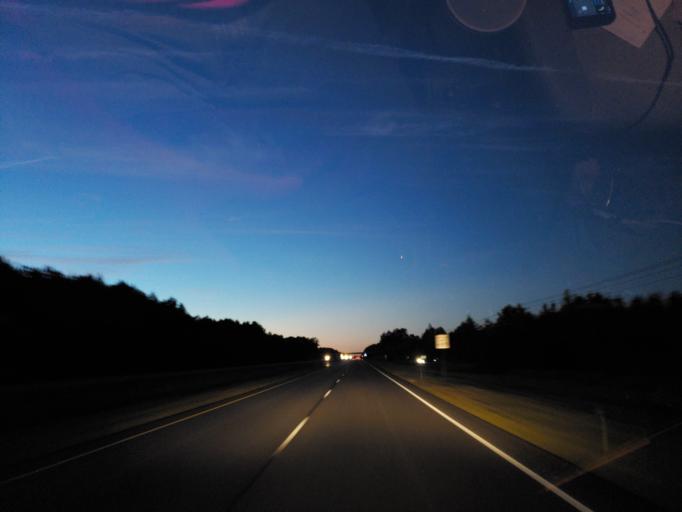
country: US
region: Mississippi
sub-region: Clarke County
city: Quitman
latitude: 32.0705
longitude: -88.6848
